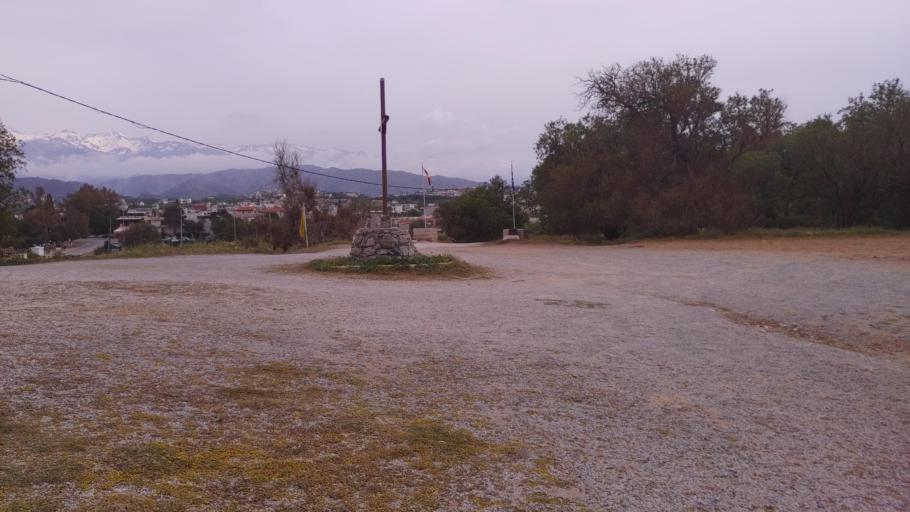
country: GR
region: Crete
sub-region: Nomos Chanias
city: Daratsos
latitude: 35.5157
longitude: 23.9776
